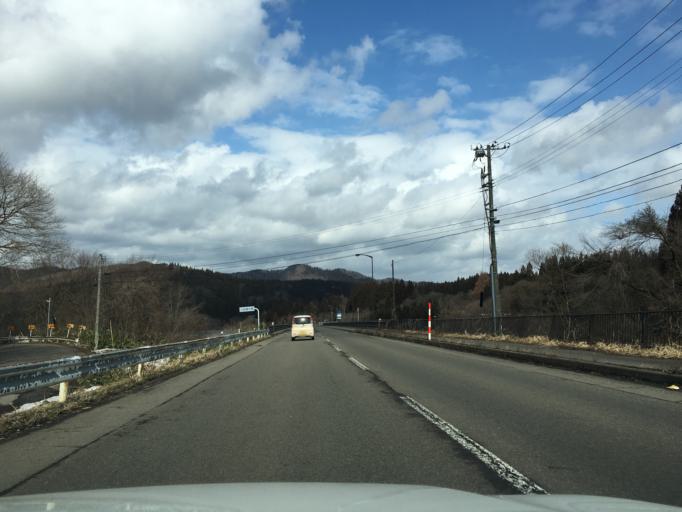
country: JP
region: Akita
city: Takanosu
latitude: 40.0233
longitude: 140.2744
